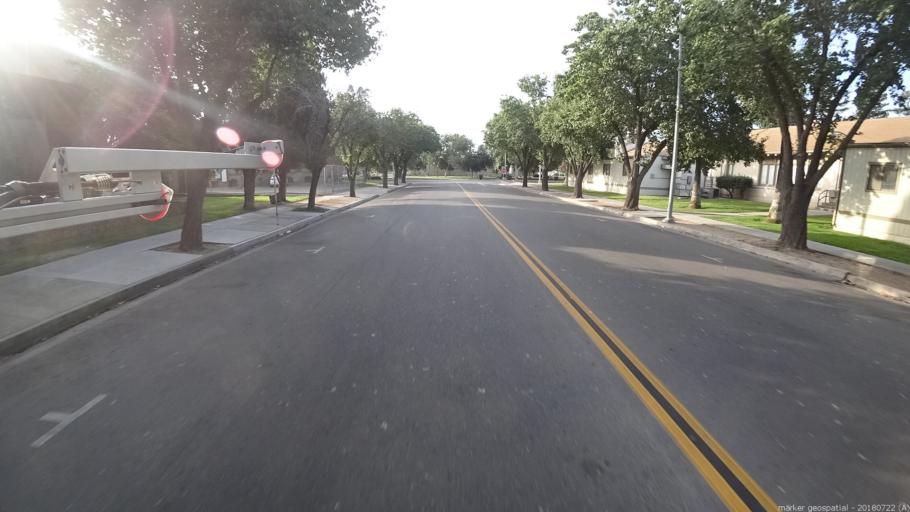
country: US
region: California
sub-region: Madera County
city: Madera
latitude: 36.9611
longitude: -120.0621
